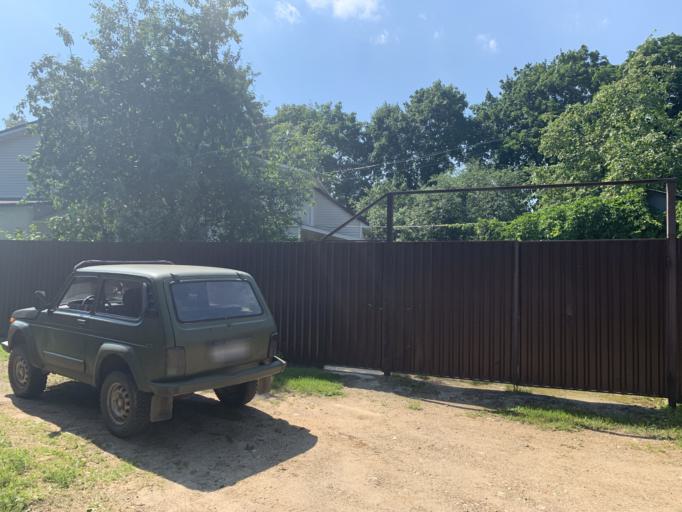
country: RU
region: Moskovskaya
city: Mamontovka
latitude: 55.9695
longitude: 37.8078
